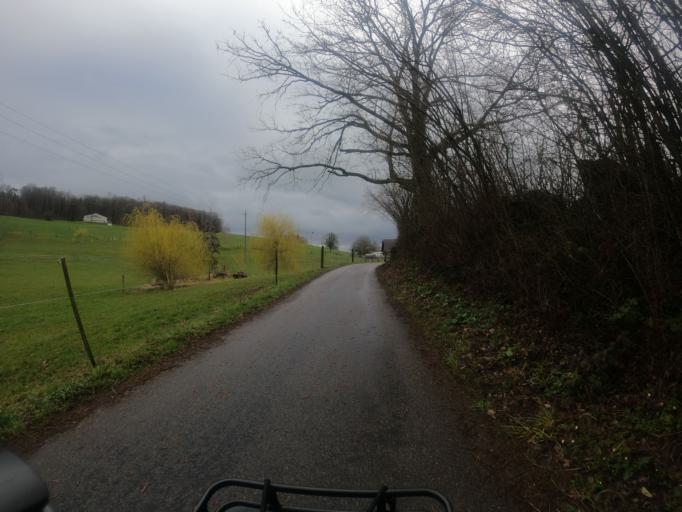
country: CH
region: Zurich
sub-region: Bezirk Affoltern
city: Mettmenstetten
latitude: 47.2577
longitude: 8.4616
